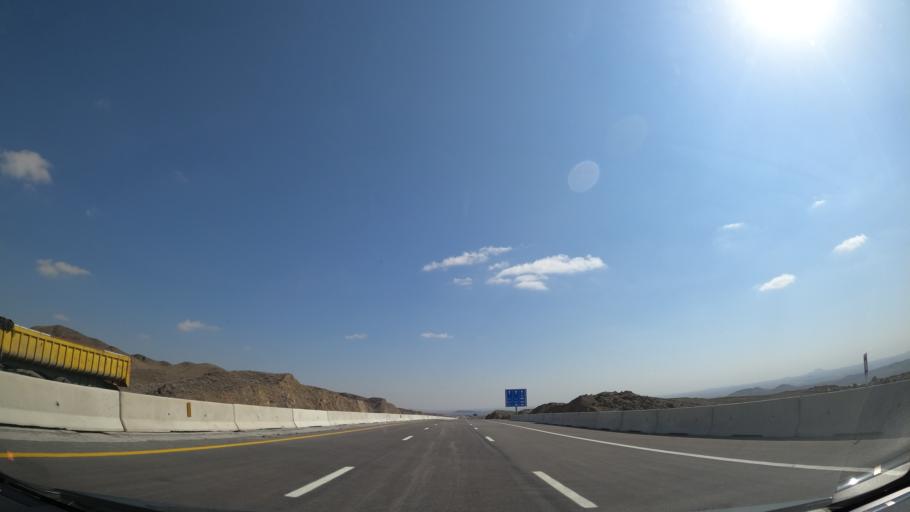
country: IR
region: Alborz
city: Nazarabad
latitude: 35.6578
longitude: 50.6622
